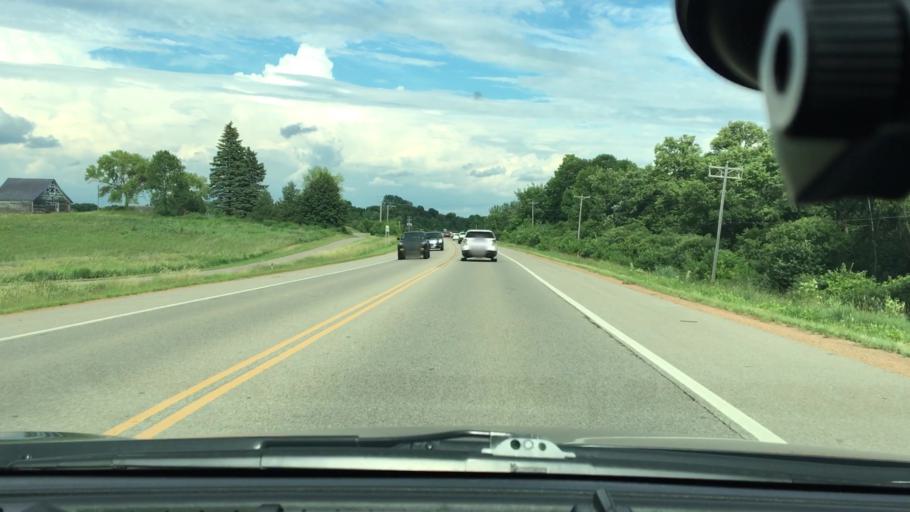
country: US
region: Minnesota
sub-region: Carver County
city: Victoria
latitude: 44.8669
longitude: -93.6319
